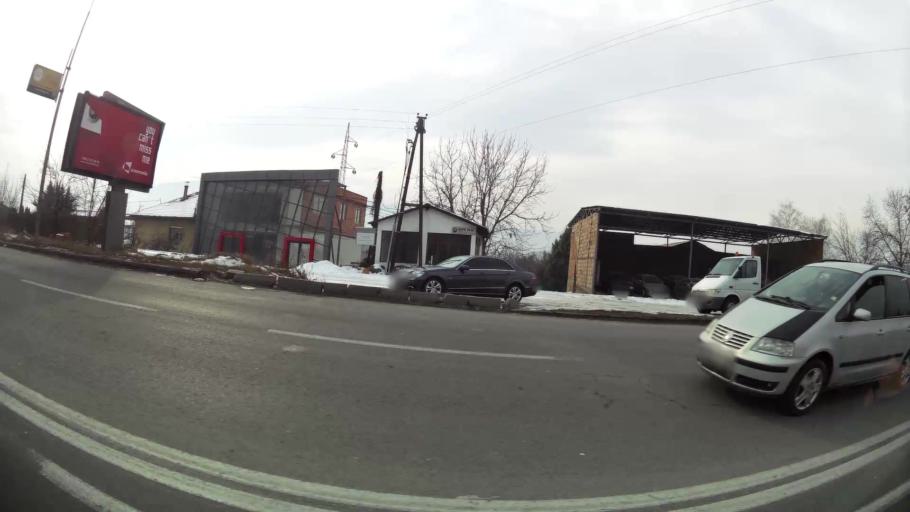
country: MK
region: Karpos
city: Skopje
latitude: 42.0152
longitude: 21.4127
